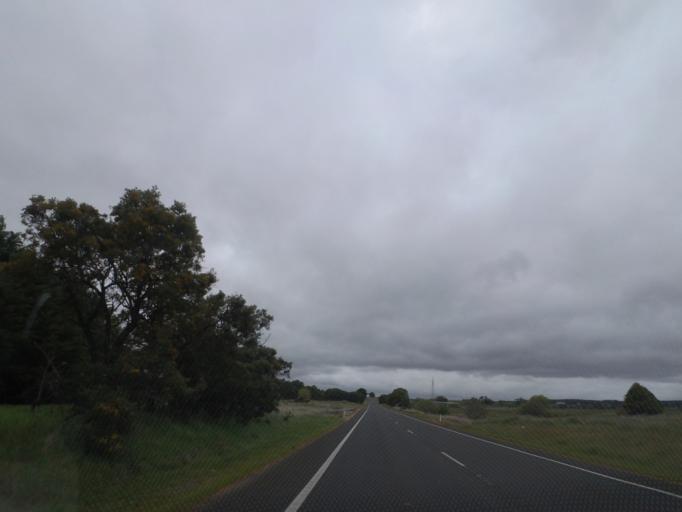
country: AU
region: Victoria
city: Brown Hill
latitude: -37.3767
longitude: 144.0228
